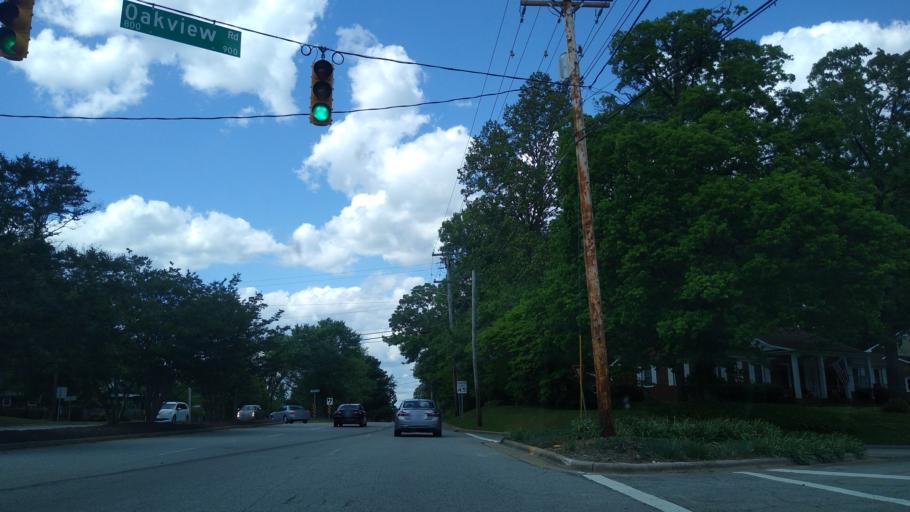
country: US
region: North Carolina
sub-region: Guilford County
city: High Point
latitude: 36.0044
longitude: -80.0100
